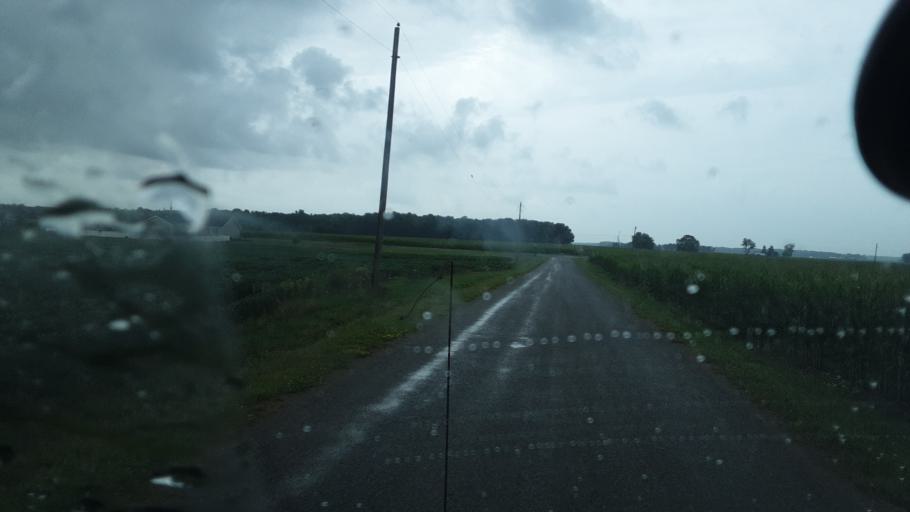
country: US
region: Indiana
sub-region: Steuben County
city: Hamilton
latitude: 41.5374
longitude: -84.8182
